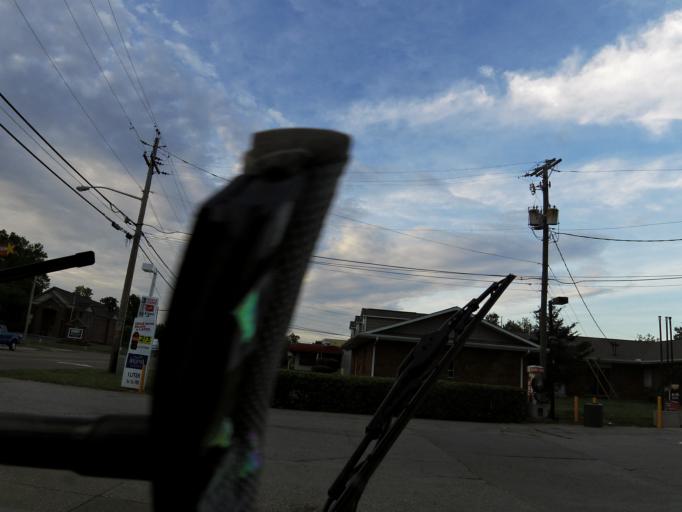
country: US
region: Tennessee
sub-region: Knox County
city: Knoxville
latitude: 36.0247
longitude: -83.9233
